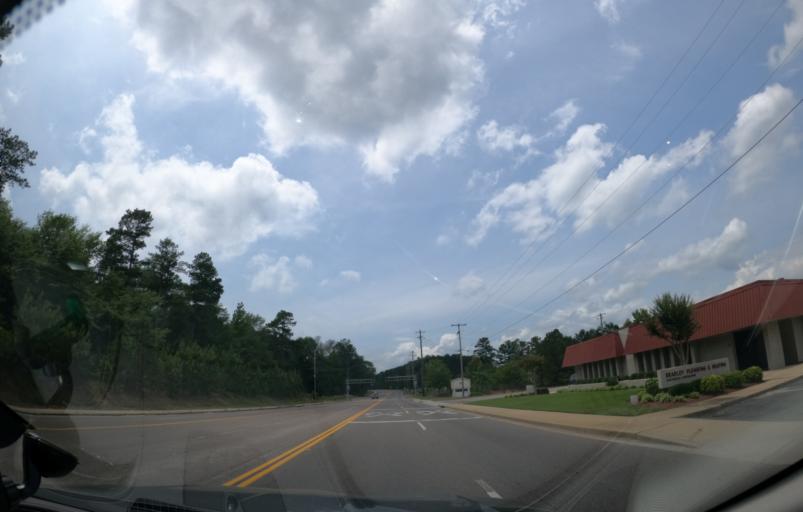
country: US
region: South Carolina
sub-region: Aiken County
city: Aiken
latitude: 33.5774
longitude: -81.7048
